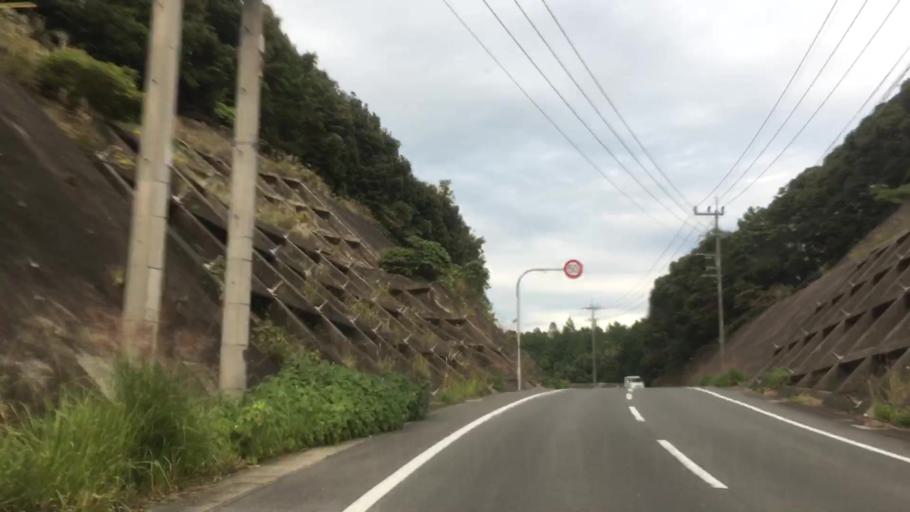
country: JP
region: Nagasaki
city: Sasebo
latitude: 32.9691
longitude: 129.6954
